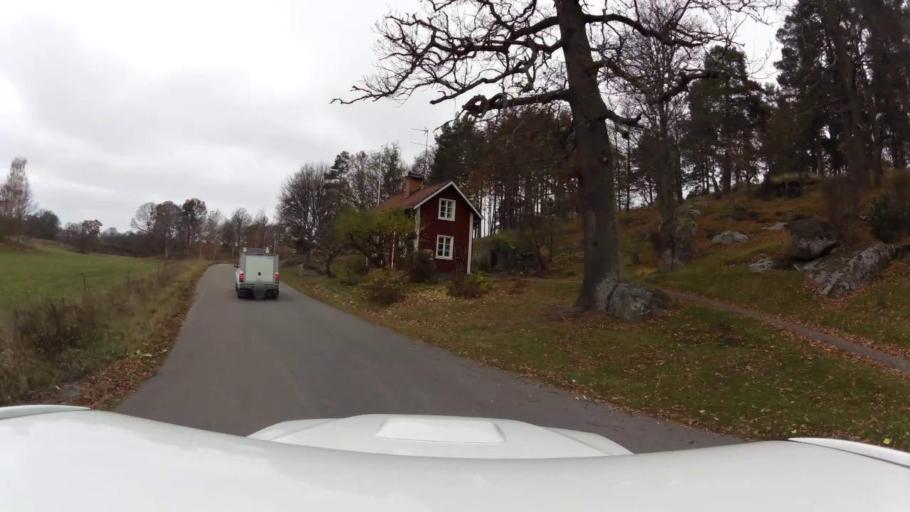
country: SE
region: OEstergoetland
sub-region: Kinda Kommun
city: Rimforsa
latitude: 58.2388
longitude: 15.6919
